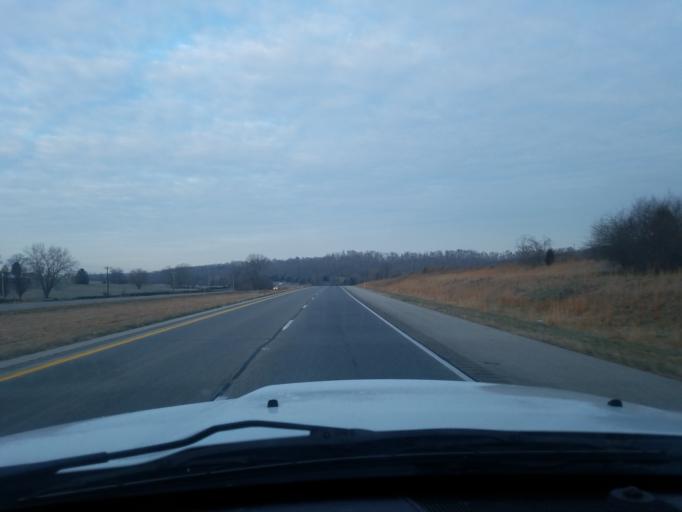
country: US
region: Indiana
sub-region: Harrison County
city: Corydon
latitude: 38.2421
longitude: -86.1964
